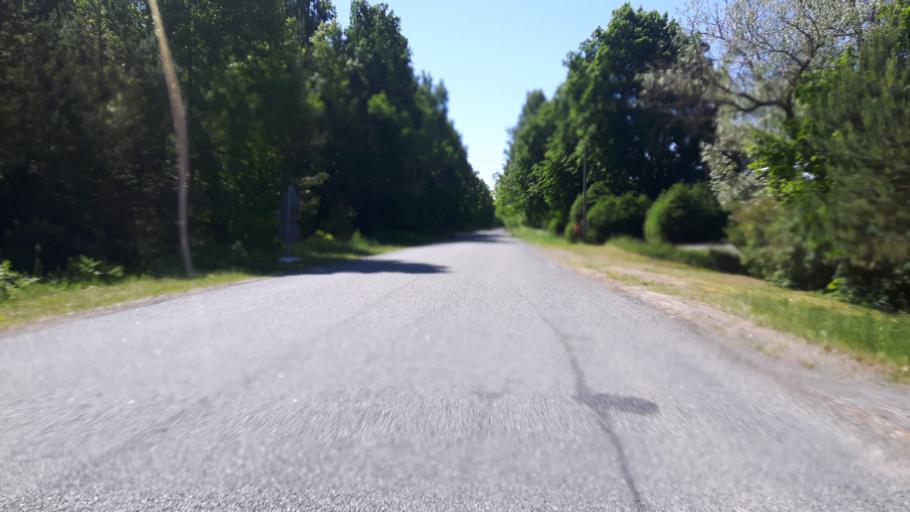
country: EE
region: Paernumaa
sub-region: Paernu linn
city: Parnu
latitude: 58.1263
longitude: 24.5086
